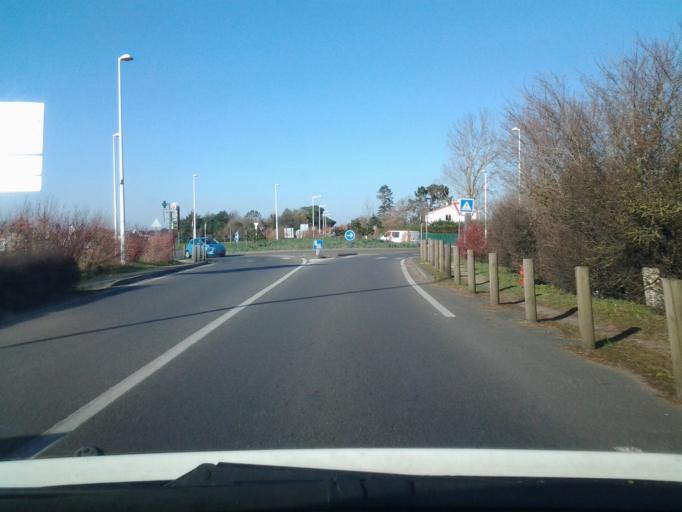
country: FR
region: Pays de la Loire
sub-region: Departement de la Vendee
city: Olonne-sur-Mer
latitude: 46.5418
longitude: -1.7704
